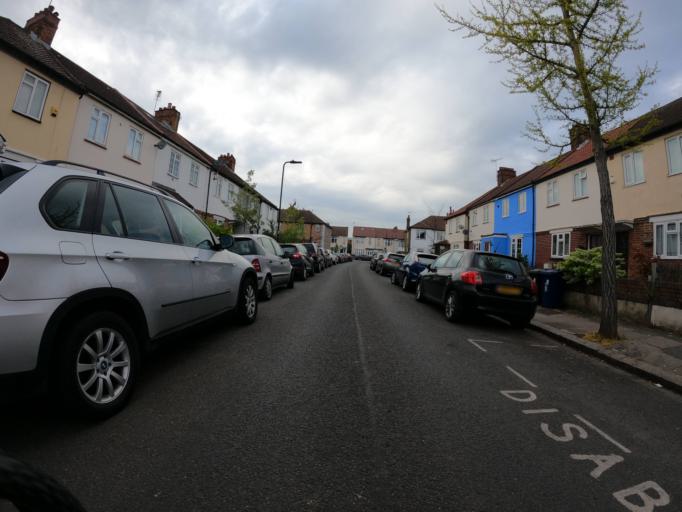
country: GB
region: England
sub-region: Greater London
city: Greenford
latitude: 51.5071
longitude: -0.3348
